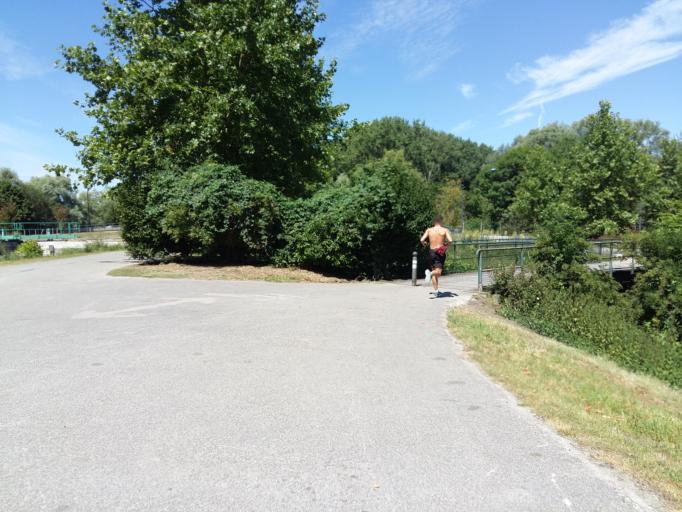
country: FR
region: Picardie
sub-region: Departement de la Somme
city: Dreuil-les-Amiens
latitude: 49.9183
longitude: 2.2587
